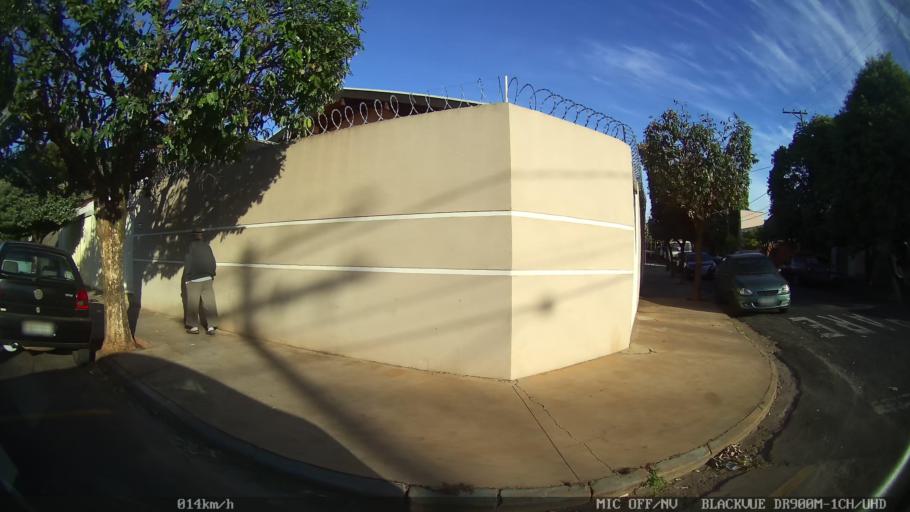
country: BR
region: Sao Paulo
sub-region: Sao Jose Do Rio Preto
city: Sao Jose do Rio Preto
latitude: -20.8252
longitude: -49.3731
